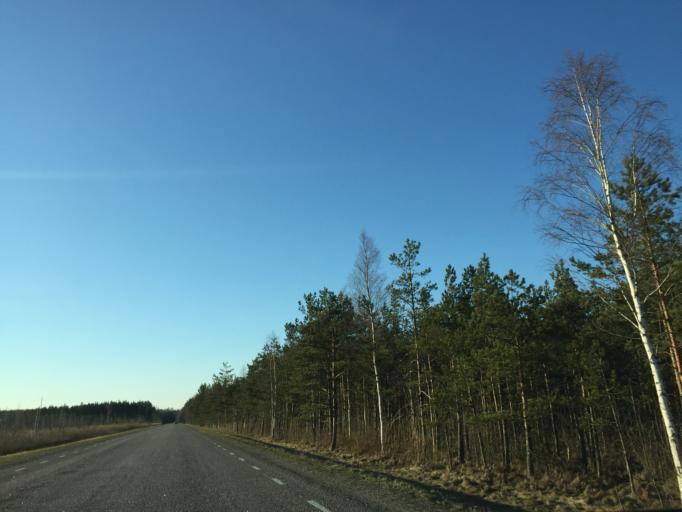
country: EE
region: Ida-Virumaa
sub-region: Toila vald
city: Voka
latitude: 59.1146
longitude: 27.6358
